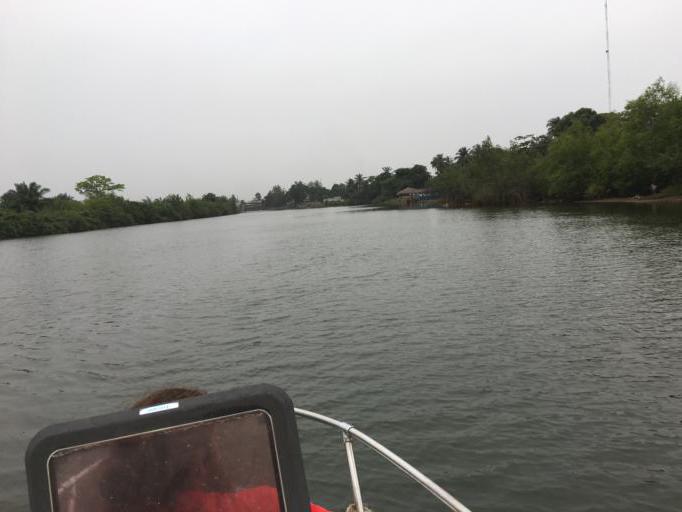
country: LR
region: Montserrado
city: Monrovia
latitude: 6.3813
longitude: -10.7806
